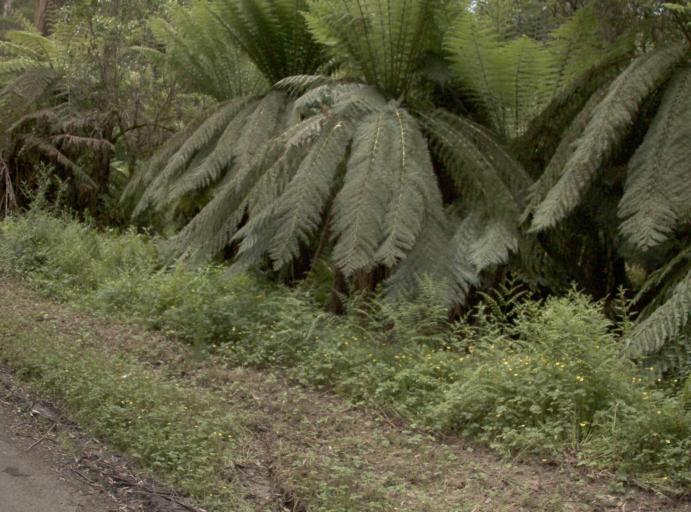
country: AU
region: Victoria
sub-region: Latrobe
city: Traralgon
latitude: -38.4240
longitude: 146.5674
